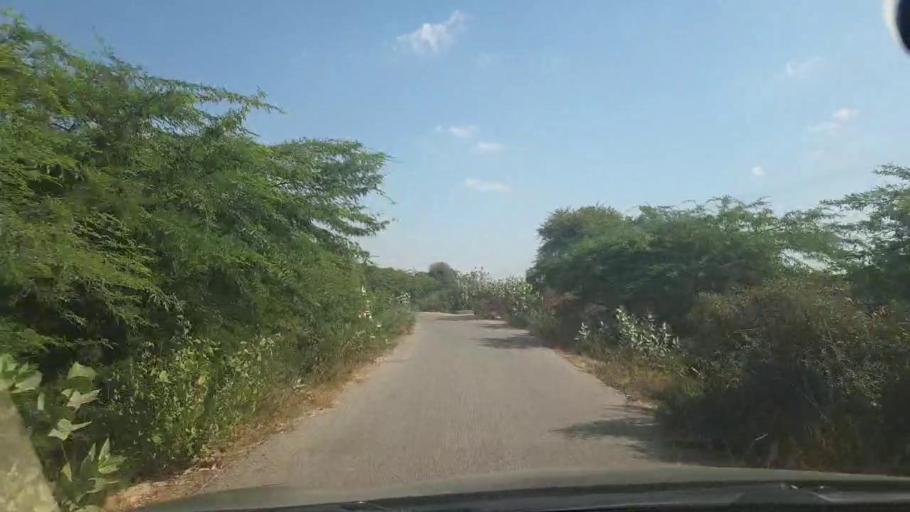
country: PK
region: Sindh
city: Malir Cantonment
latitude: 25.0565
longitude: 67.3905
